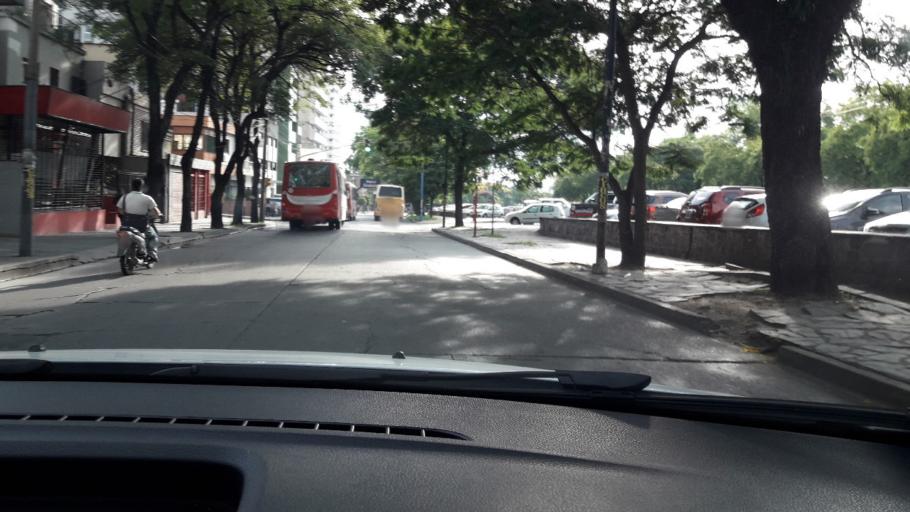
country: AR
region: Jujuy
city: San Salvador de Jujuy
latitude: -24.1887
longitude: -65.3005
